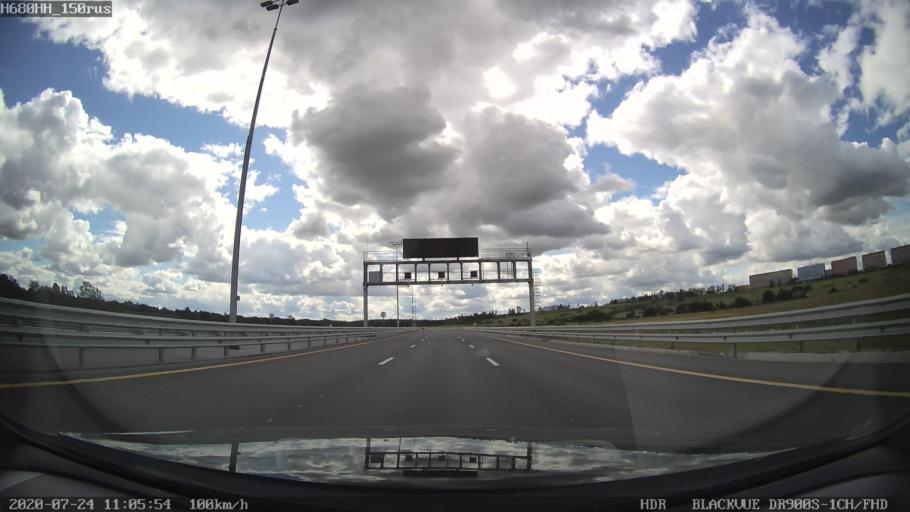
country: RU
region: St.-Petersburg
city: Shushary
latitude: 59.7708
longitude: 30.3637
